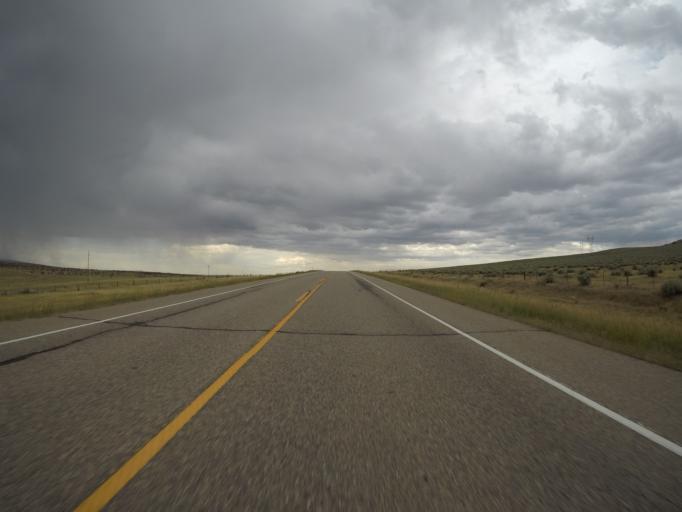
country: US
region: Colorado
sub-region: Rio Blanco County
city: Rangely
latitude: 40.3723
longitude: -108.3829
